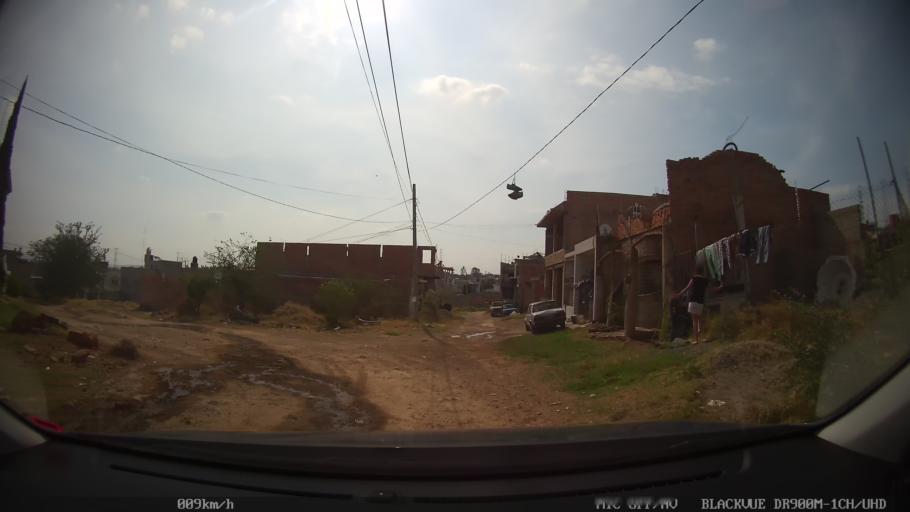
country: MX
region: Jalisco
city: Tonala
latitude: 20.6409
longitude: -103.2318
